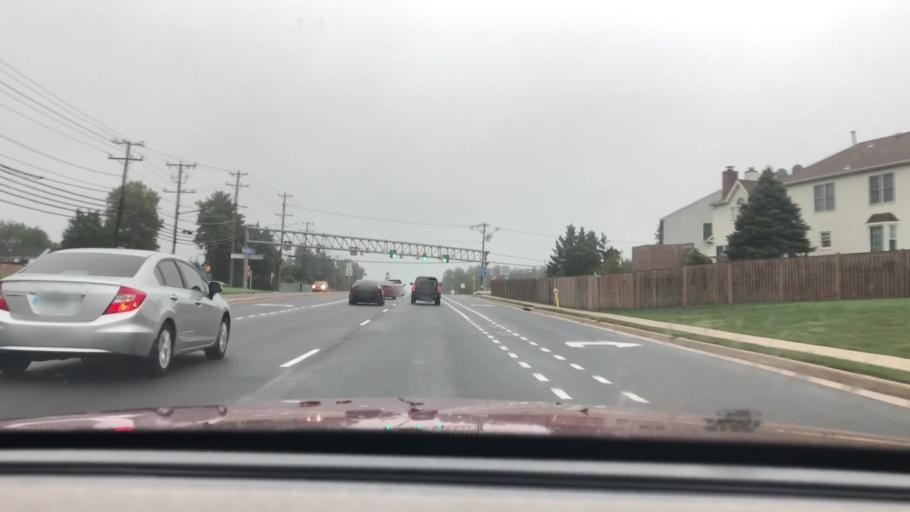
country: US
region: Virginia
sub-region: Fairfax County
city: Greenbriar
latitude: 38.8766
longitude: -77.4089
